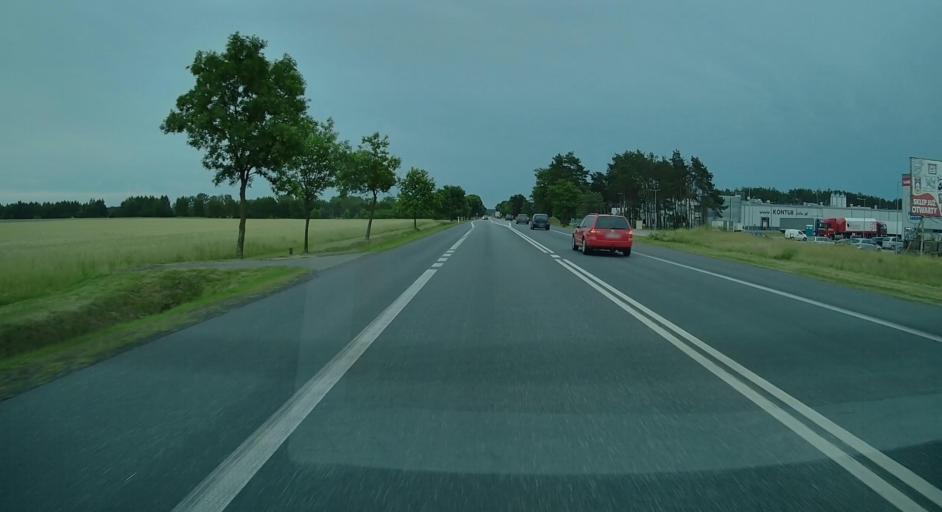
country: PL
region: Lublin Voivodeship
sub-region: Powiat bialski
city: Rokitno
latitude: 52.0354
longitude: 23.2517
